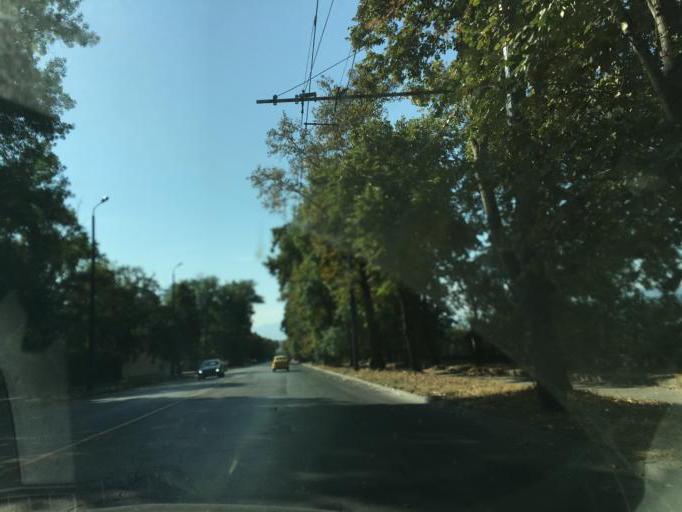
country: BG
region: Pazardzhik
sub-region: Obshtina Pazardzhik
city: Pazardzhik
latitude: 42.1791
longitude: 24.3198
